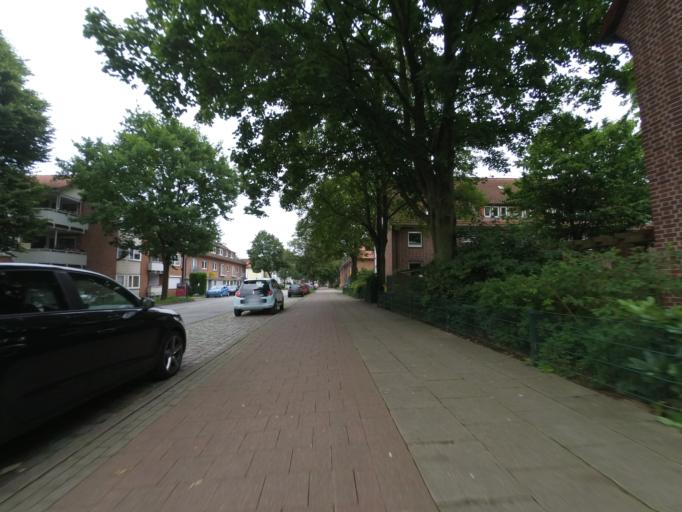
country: DE
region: Hamburg
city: Bergedorf
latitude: 53.5005
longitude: 10.1989
